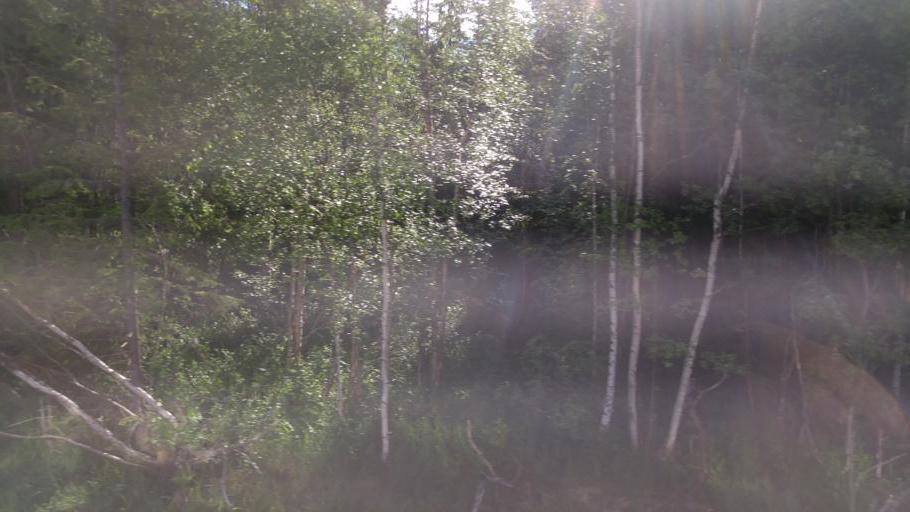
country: NO
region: Nord-Trondelag
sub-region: Meraker
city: Meraker
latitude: 63.3955
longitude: 11.8440
